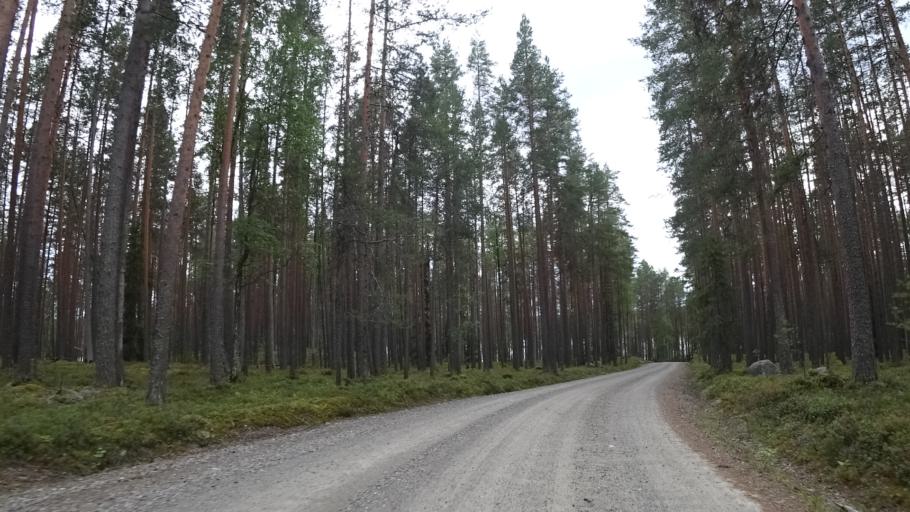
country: FI
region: North Karelia
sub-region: Joensuu
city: Ilomantsi
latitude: 62.5904
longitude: 31.1818
